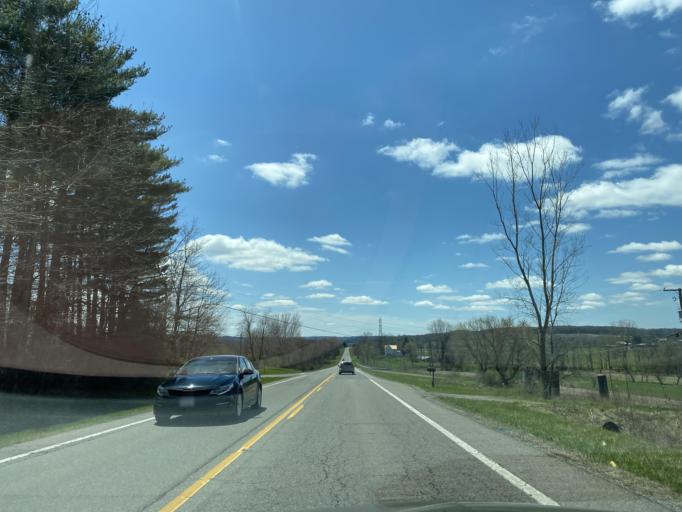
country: US
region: Ohio
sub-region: Wayne County
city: Shreve
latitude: 40.7341
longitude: -81.9917
